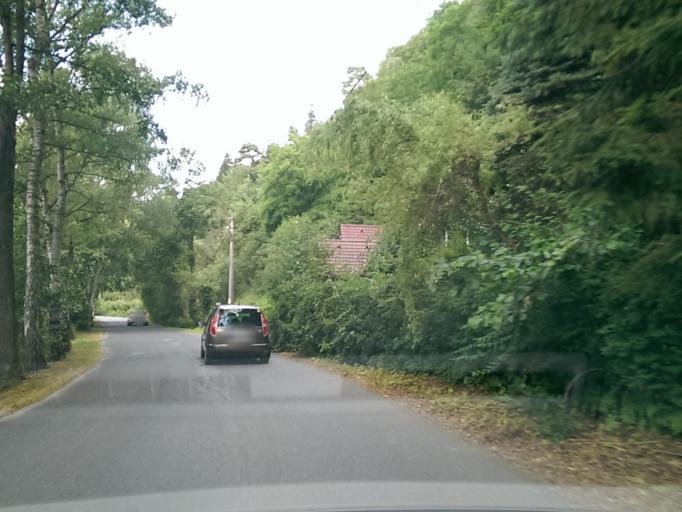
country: CZ
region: Central Bohemia
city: Mseno
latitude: 50.4321
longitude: 14.5825
